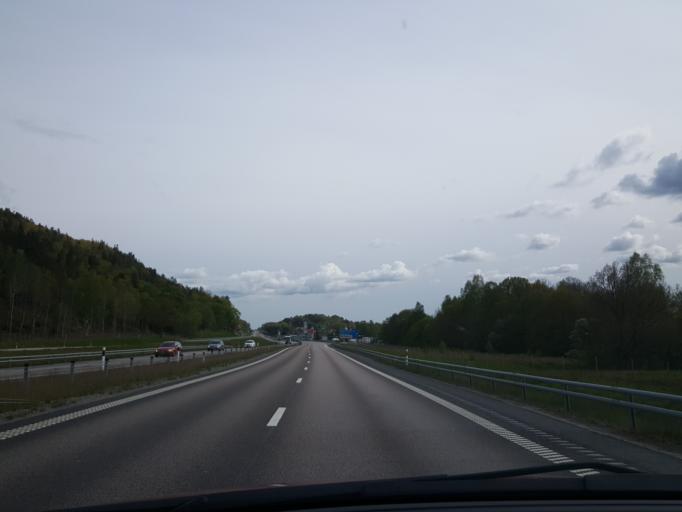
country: SE
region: Vaestra Goetaland
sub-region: Lilla Edets Kommun
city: Lilla Edet
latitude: 58.1532
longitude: 12.1351
